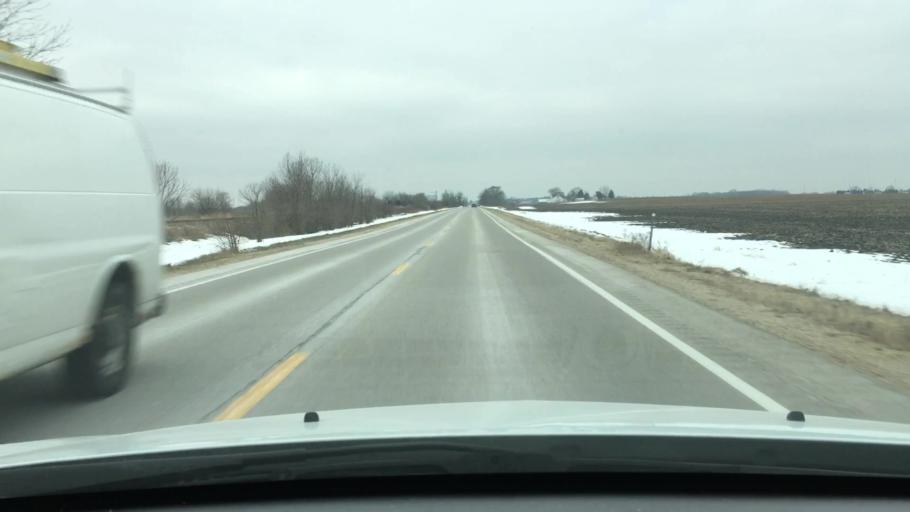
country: US
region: Illinois
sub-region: DeKalb County
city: Waterman
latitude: 41.7695
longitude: -88.7212
